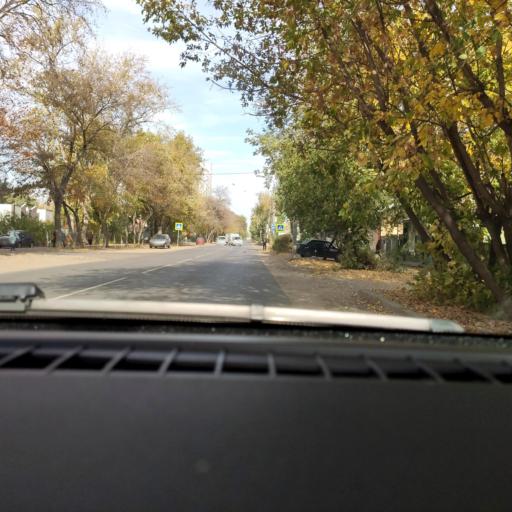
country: RU
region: Voronezj
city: Voronezh
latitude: 51.6382
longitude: 39.1875
